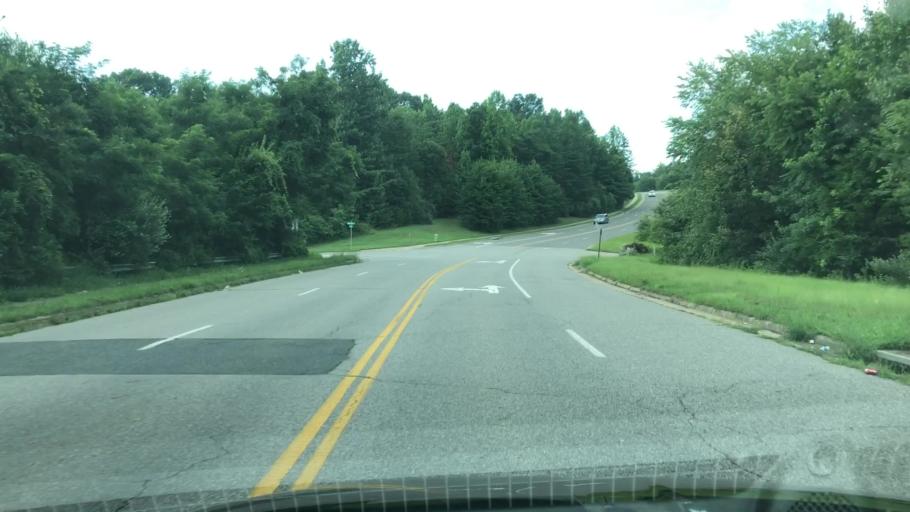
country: US
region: Virginia
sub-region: Stafford County
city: Falmouth
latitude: 38.3631
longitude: -77.5288
